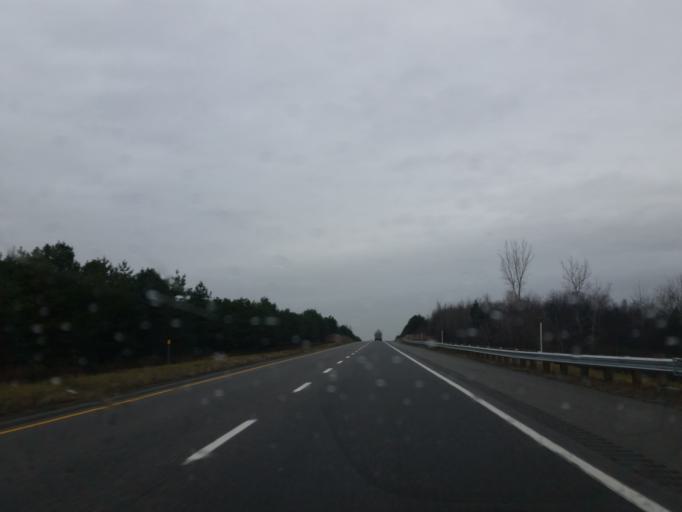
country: CA
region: Quebec
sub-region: Mauricie
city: Becancour
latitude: 46.5241
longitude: -72.2854
